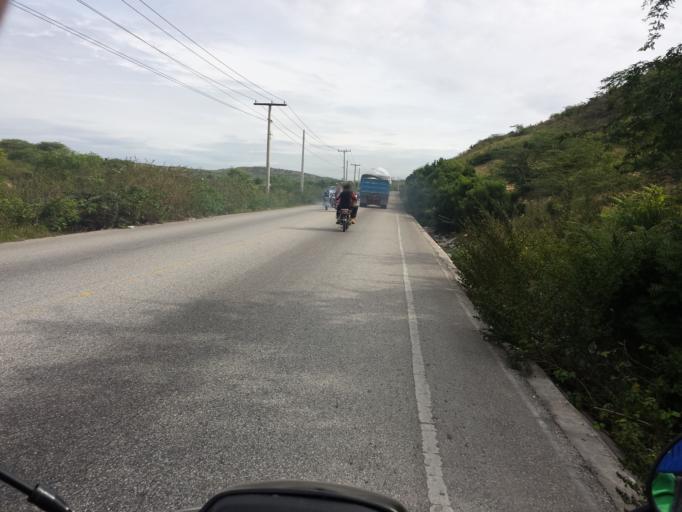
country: HT
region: Artibonite
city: Saint-Marc
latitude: 19.1350
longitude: -72.6761
